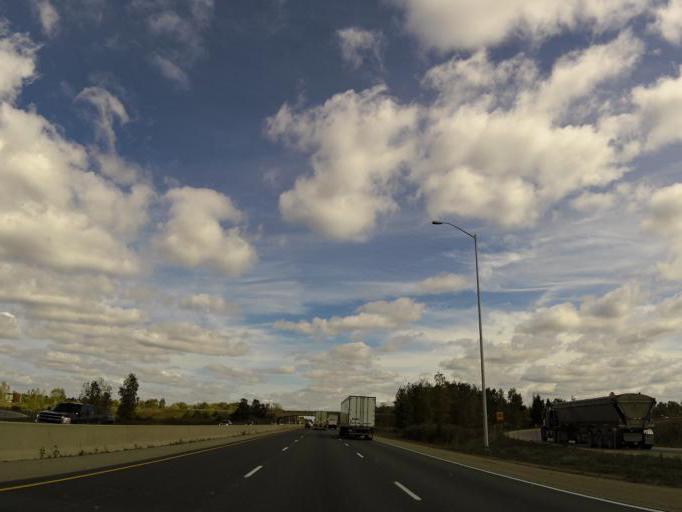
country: CA
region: Ontario
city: Dorchester
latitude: 42.9648
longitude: -81.0206
